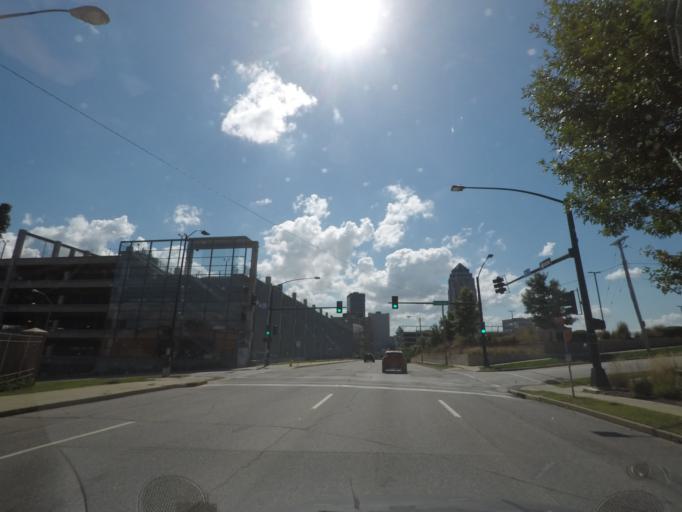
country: US
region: Iowa
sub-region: Polk County
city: Des Moines
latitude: 41.5937
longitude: -93.6269
